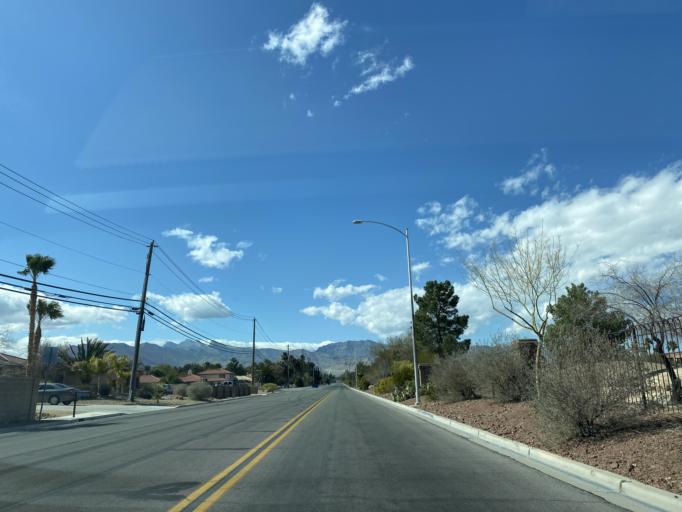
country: US
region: Nevada
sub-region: Clark County
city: Spring Valley
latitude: 36.2555
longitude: -115.2635
